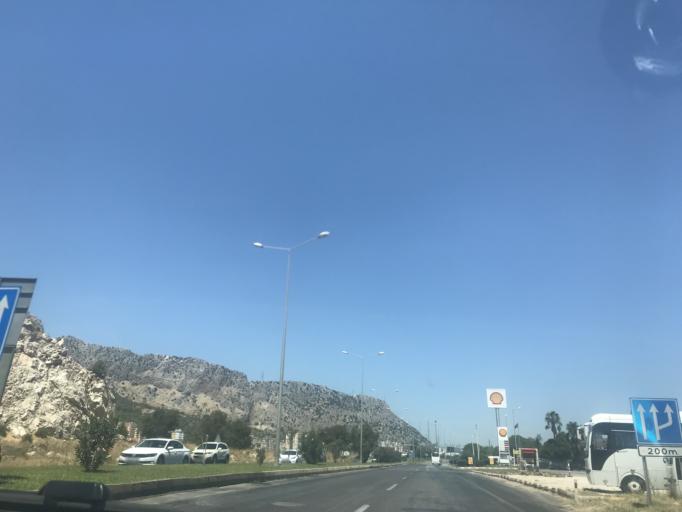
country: TR
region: Antalya
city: Cakirlar
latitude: 36.8323
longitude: 30.5954
